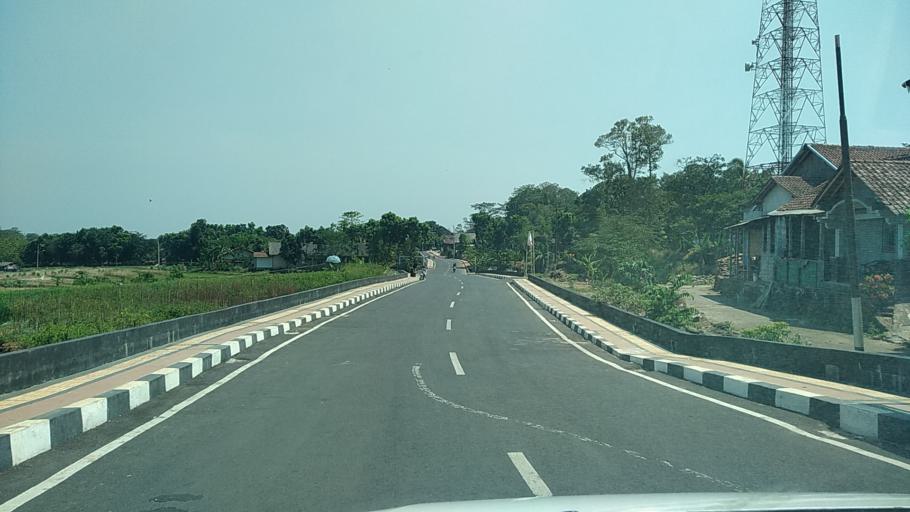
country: ID
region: Central Java
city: Ungaran
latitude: -7.0889
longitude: 110.3597
